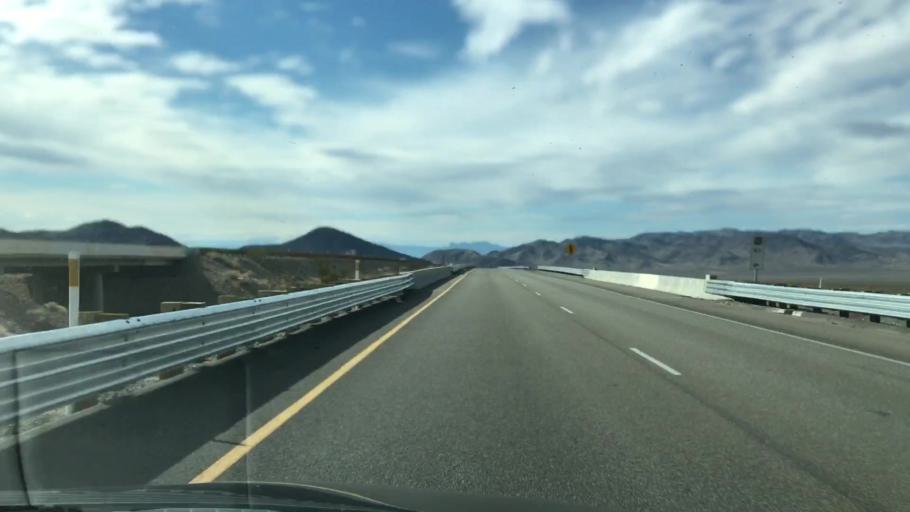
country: US
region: Nevada
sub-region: Nye County
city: Pahrump
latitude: 36.5983
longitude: -115.9973
